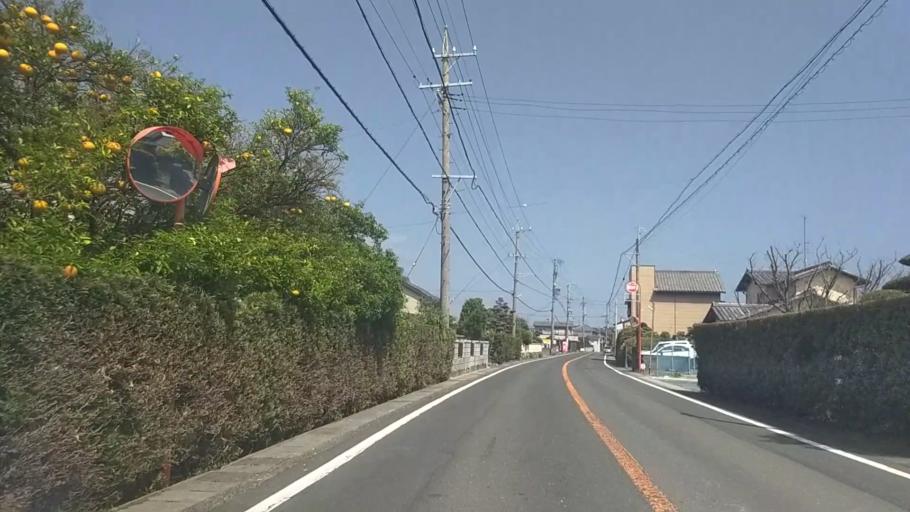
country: JP
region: Shizuoka
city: Hamamatsu
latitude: 34.6812
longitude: 137.7043
